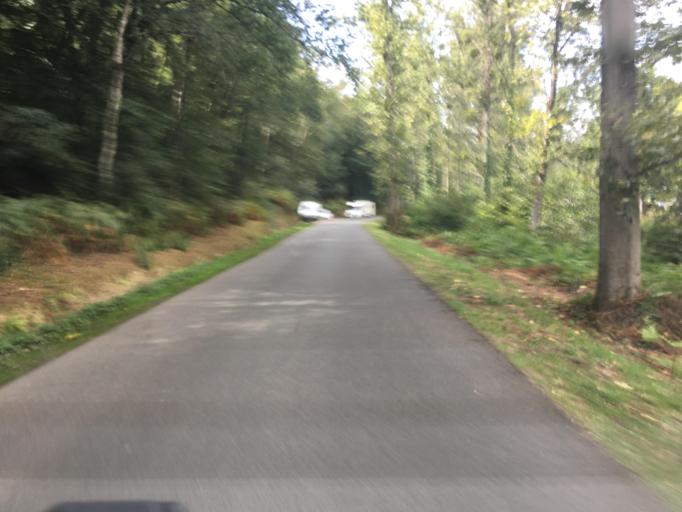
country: FR
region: Brittany
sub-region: Departement des Cotes-d'Armor
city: Gouarec
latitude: 48.2103
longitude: -3.1274
